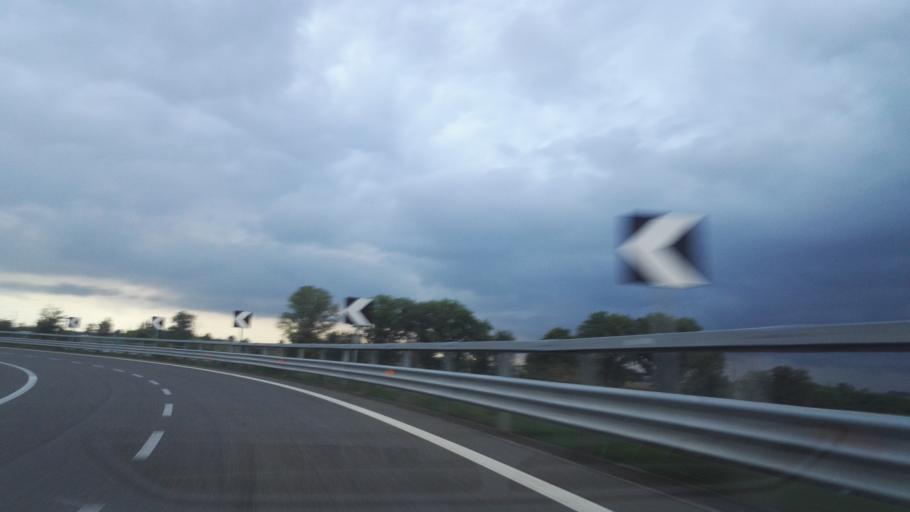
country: IT
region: Lombardy
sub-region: Citta metropolitana di Milano
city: Liscate
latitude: 45.4678
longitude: 9.4363
